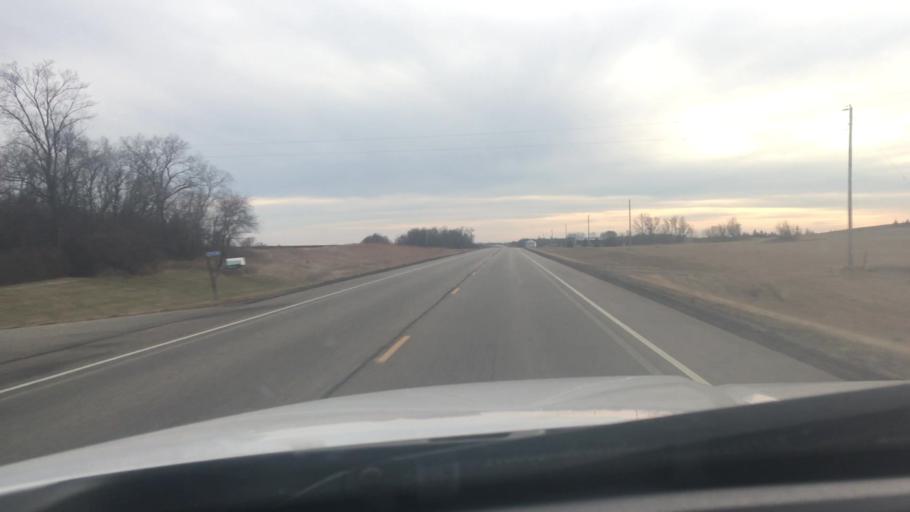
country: US
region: Minnesota
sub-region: Otter Tail County
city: Perham
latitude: 46.3299
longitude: -95.7185
